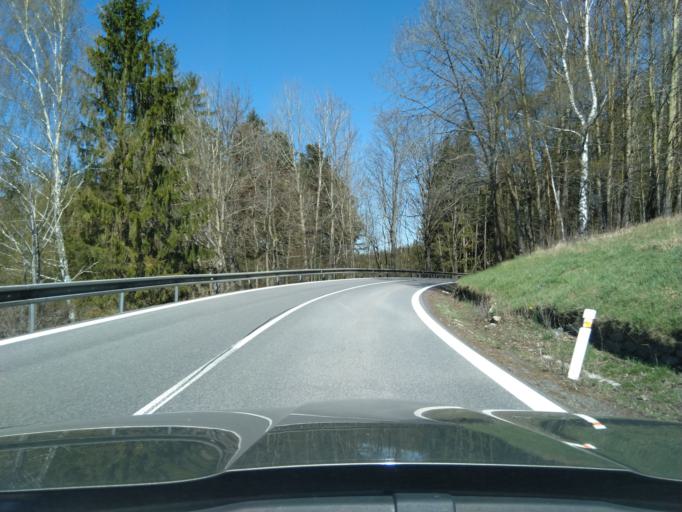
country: CZ
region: Jihocesky
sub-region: Okres Prachatice
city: Vimperk
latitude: 49.0356
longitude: 13.7618
